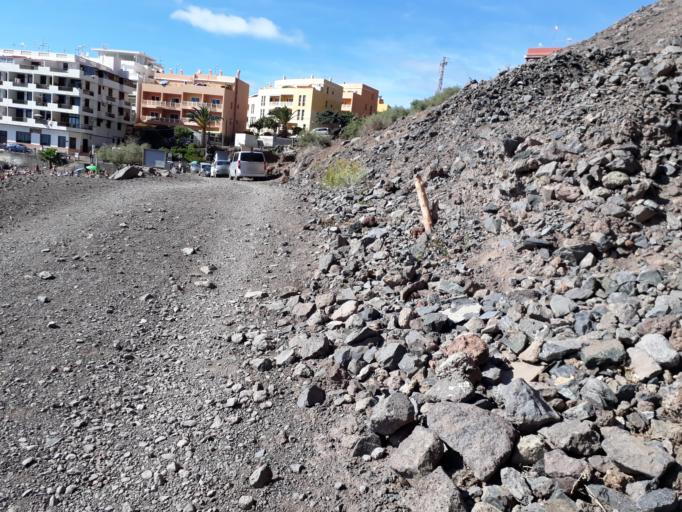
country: ES
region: Canary Islands
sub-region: Provincia de Santa Cruz de Tenerife
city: Alajero
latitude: 28.0827
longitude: -17.3313
